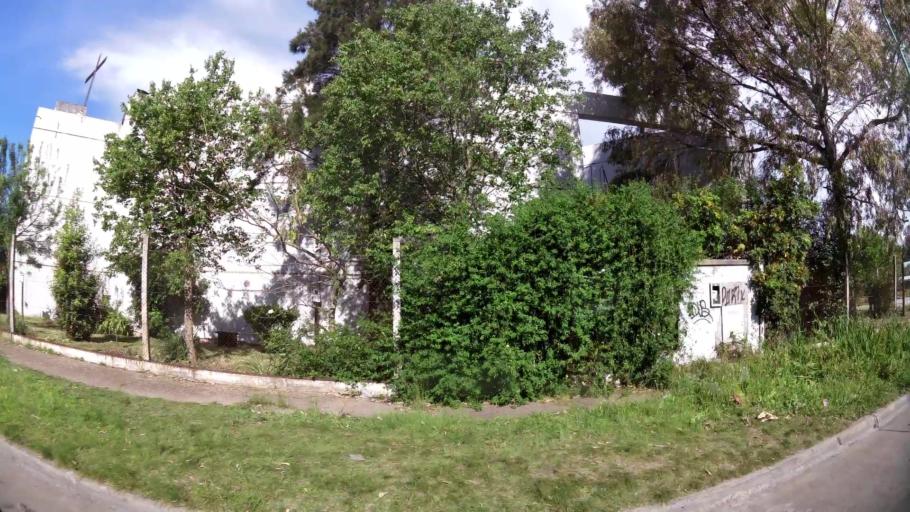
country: AR
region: Buenos Aires
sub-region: Partido de Almirante Brown
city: Adrogue
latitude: -34.8188
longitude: -58.3466
